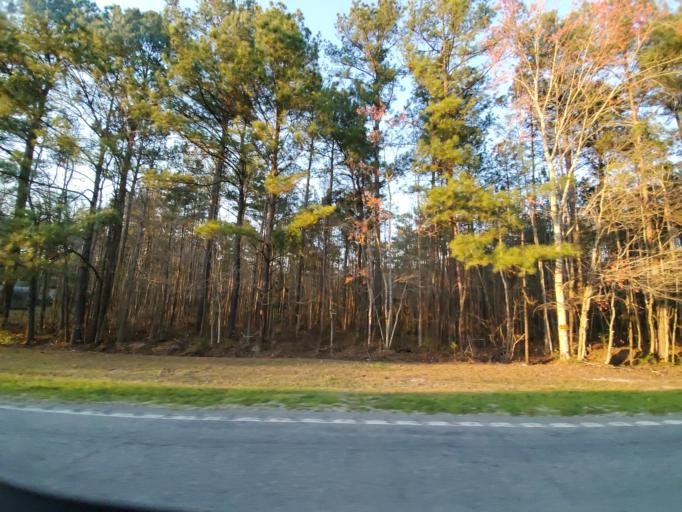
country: US
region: South Carolina
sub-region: Dorchester County
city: Ridgeville
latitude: 33.0433
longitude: -80.4389
